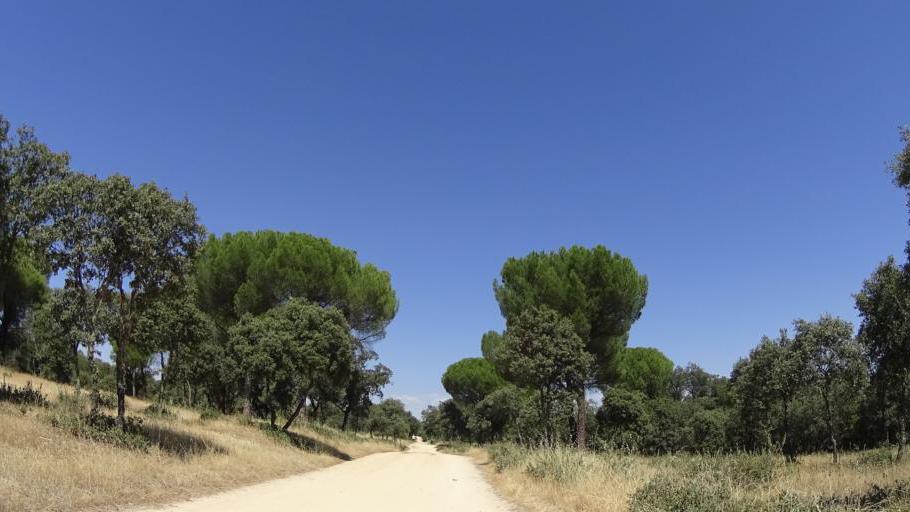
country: ES
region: Madrid
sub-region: Provincia de Madrid
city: Majadahonda
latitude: 40.4394
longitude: -3.8627
